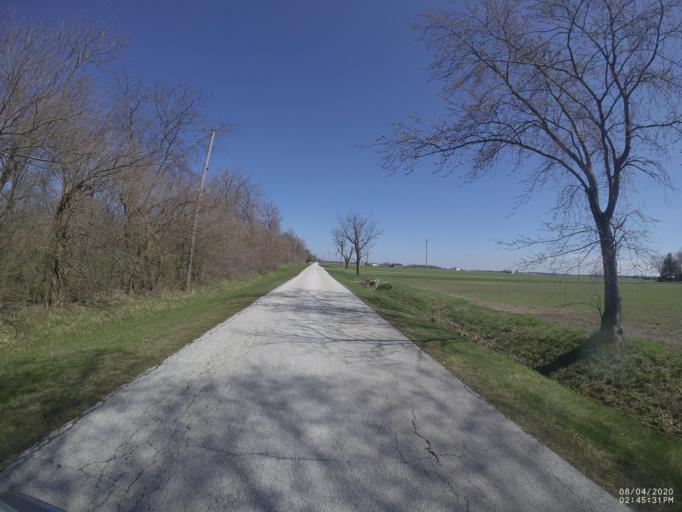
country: US
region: Ohio
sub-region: Sandusky County
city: Gibsonburg
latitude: 41.2975
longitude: -83.2911
